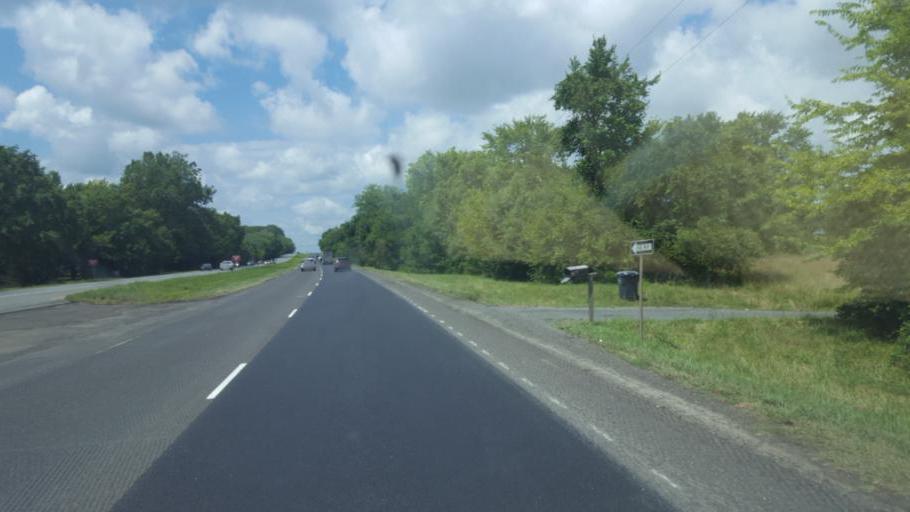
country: US
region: Virginia
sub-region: Fauquier County
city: Bealeton
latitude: 38.6020
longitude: -77.7779
